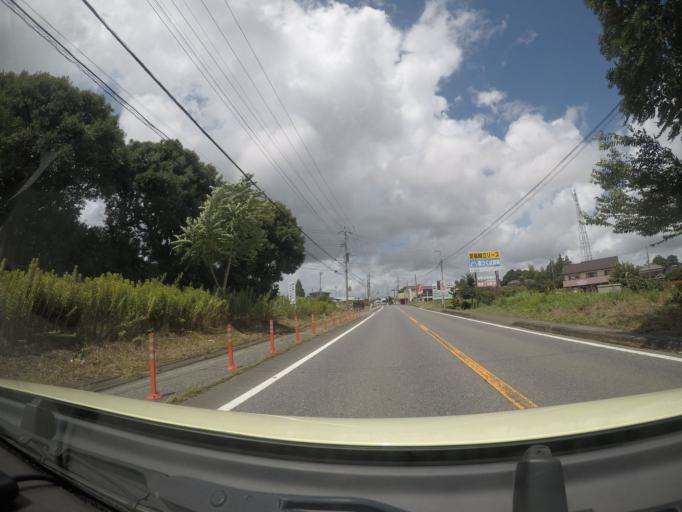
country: JP
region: Ibaraki
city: Mitsukaido
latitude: 36.0318
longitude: 139.9463
